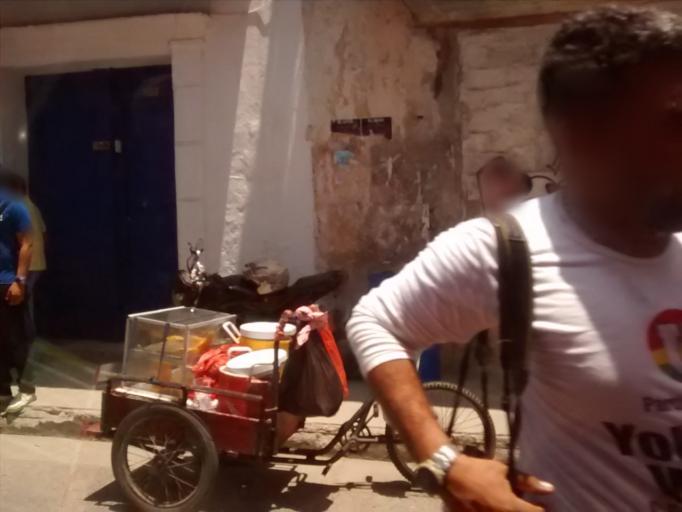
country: CO
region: Bolivar
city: Cartagena
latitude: 10.4192
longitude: -75.5467
